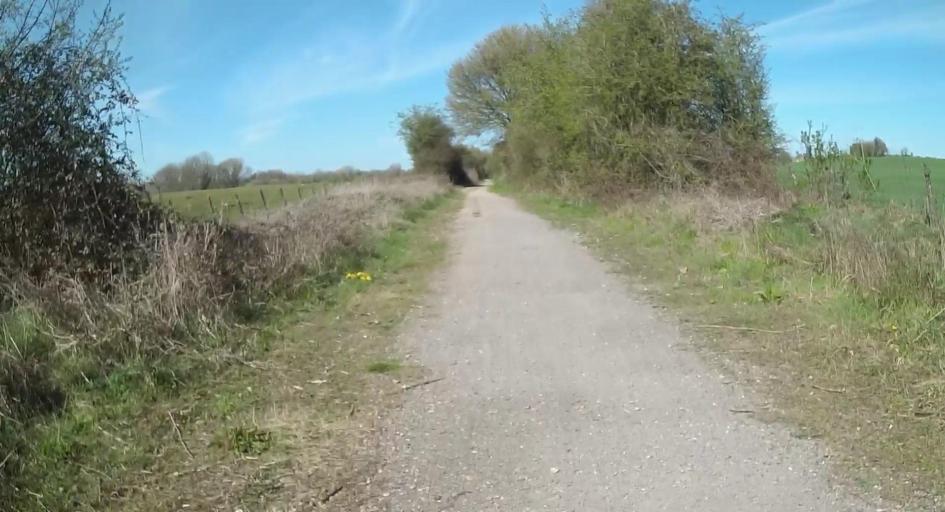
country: GB
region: England
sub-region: Hampshire
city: Romsey
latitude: 51.0627
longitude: -1.5146
